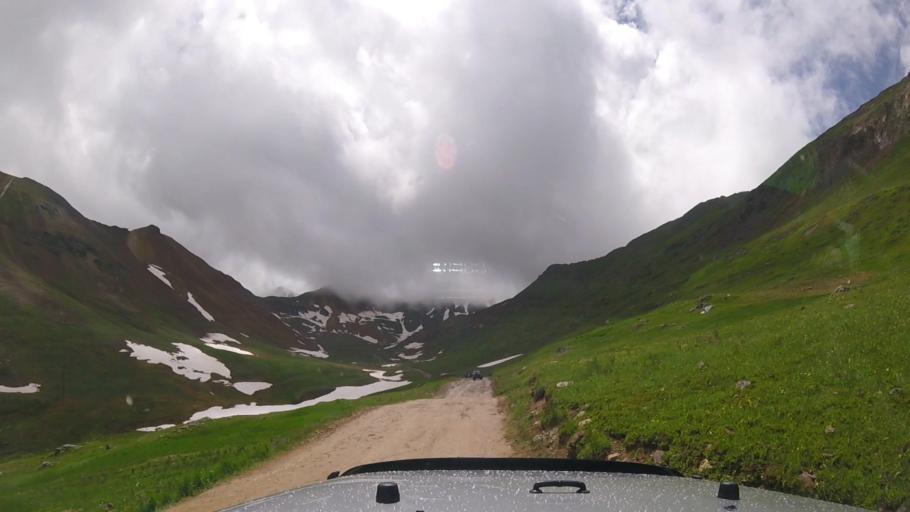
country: US
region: Colorado
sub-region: Ouray County
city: Ouray
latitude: 37.9251
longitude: -107.6104
